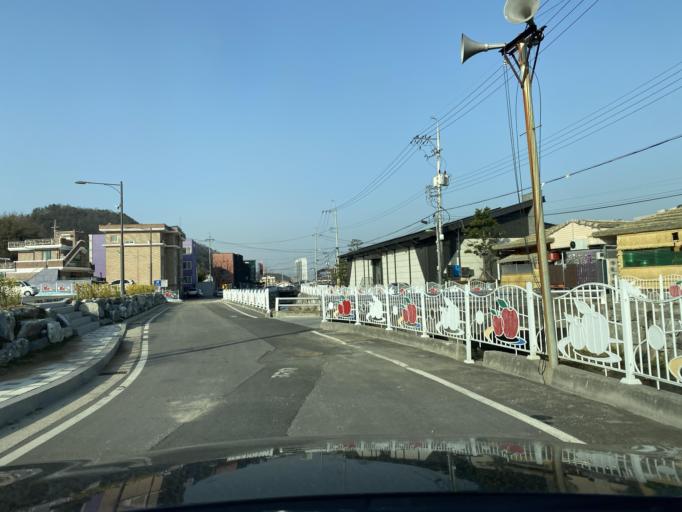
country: KR
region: Chungcheongnam-do
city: Yesan
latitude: 36.6758
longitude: 126.8486
